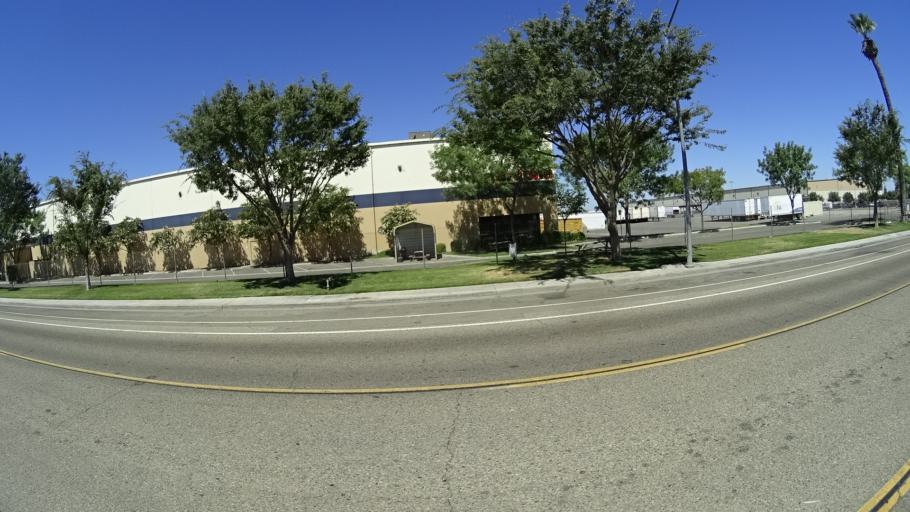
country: US
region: California
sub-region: Fresno County
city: Easton
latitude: 36.6875
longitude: -119.7727
